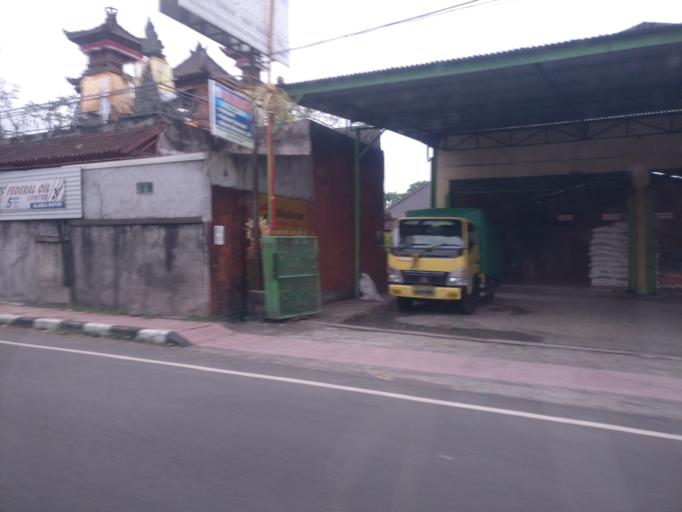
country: ID
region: Bali
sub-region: Kabupaten Gianyar
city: Ubud
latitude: -8.5599
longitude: 115.3015
